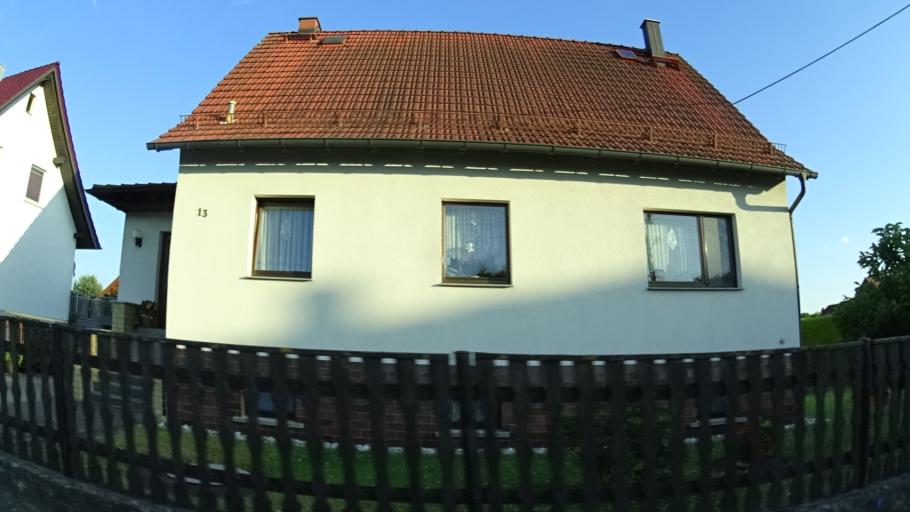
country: DE
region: Thuringia
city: Wolfershausen
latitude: 50.4542
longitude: 10.4343
